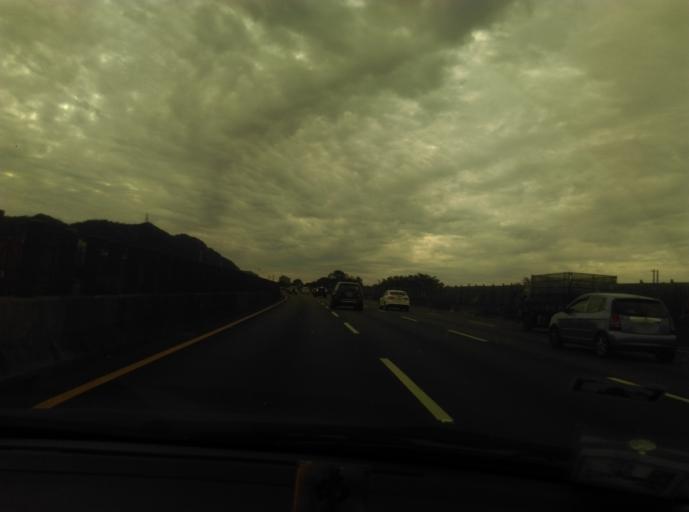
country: TW
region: Taiwan
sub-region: Taoyuan
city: Taoyuan
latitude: 24.9488
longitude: 121.3720
